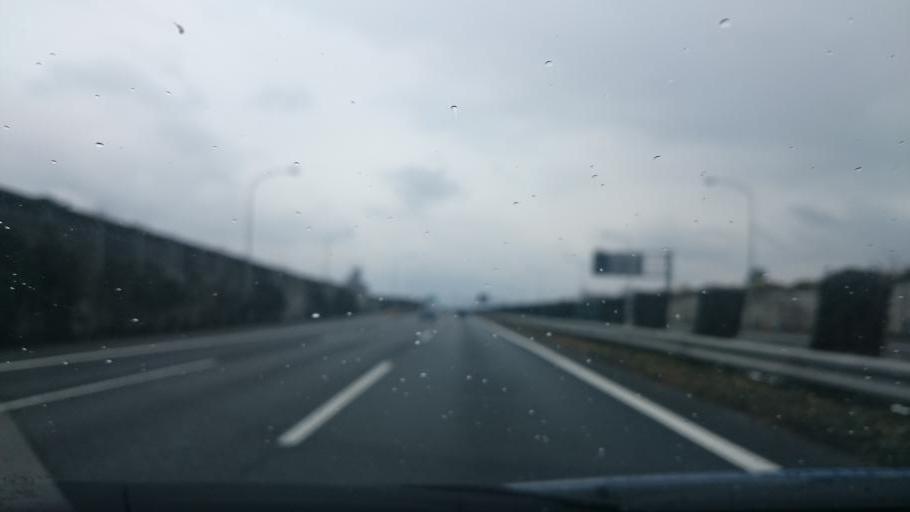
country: JP
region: Saitama
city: Sakado
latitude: 35.9503
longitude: 139.3923
